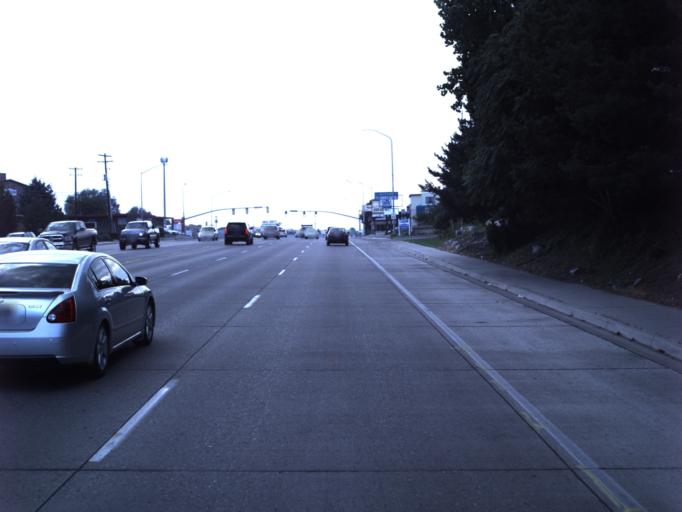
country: US
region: Utah
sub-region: Utah County
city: Provo
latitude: 40.2633
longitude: -111.6787
